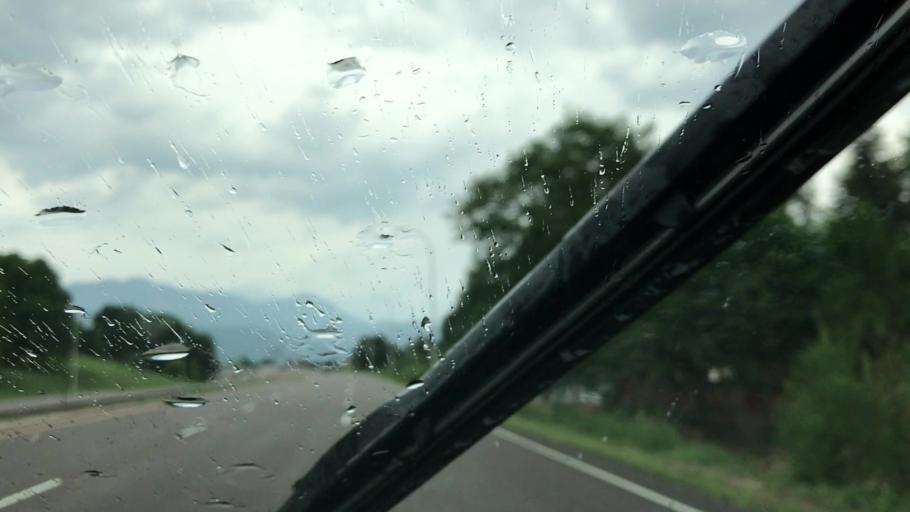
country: US
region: Colorado
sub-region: El Paso County
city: Colorado Springs
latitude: 38.7971
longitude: -104.8128
